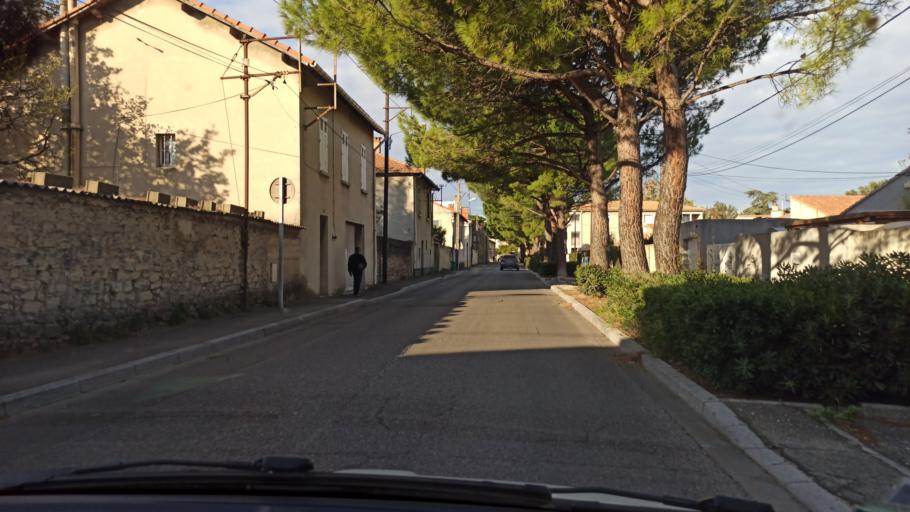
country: FR
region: Provence-Alpes-Cote d'Azur
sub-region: Departement du Vaucluse
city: Montfavet
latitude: 43.9362
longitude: 4.8747
